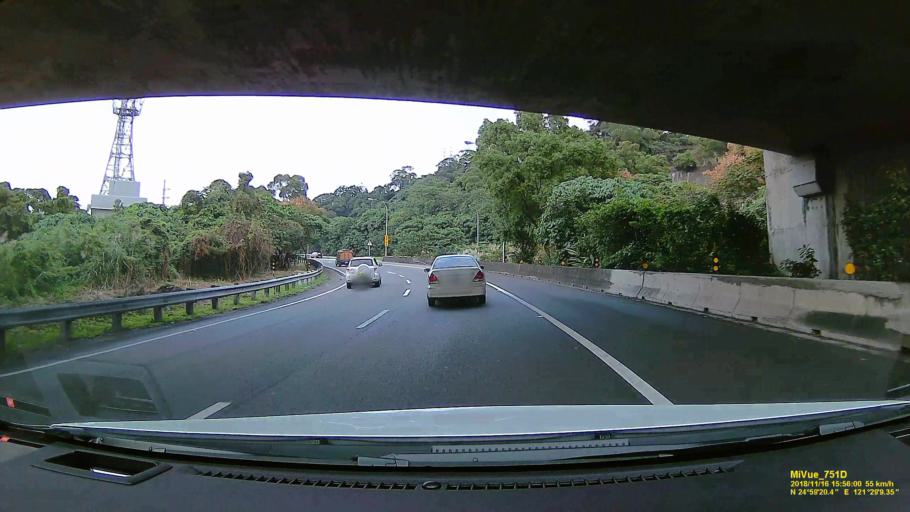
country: TW
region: Taipei
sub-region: Taipei
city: Banqiao
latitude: 24.9891
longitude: 121.4860
